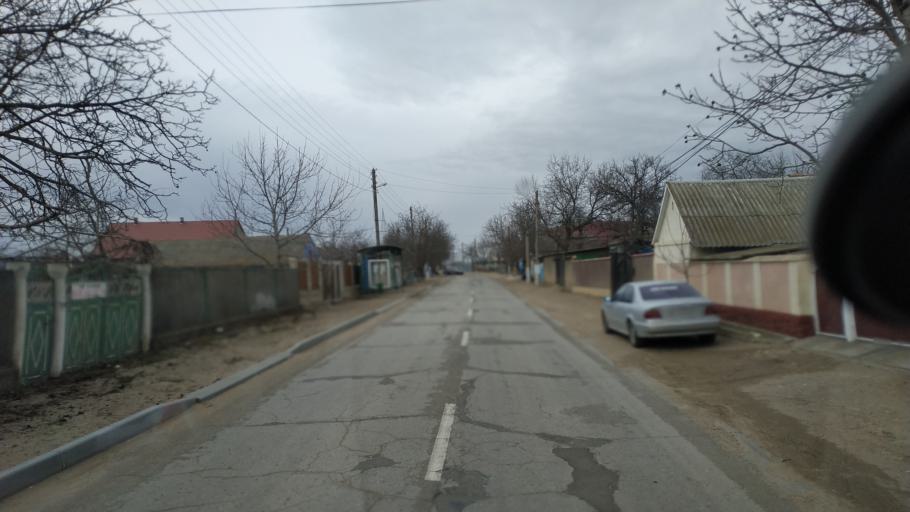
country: MD
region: Telenesti
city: Cocieri
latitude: 47.3158
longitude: 29.1042
